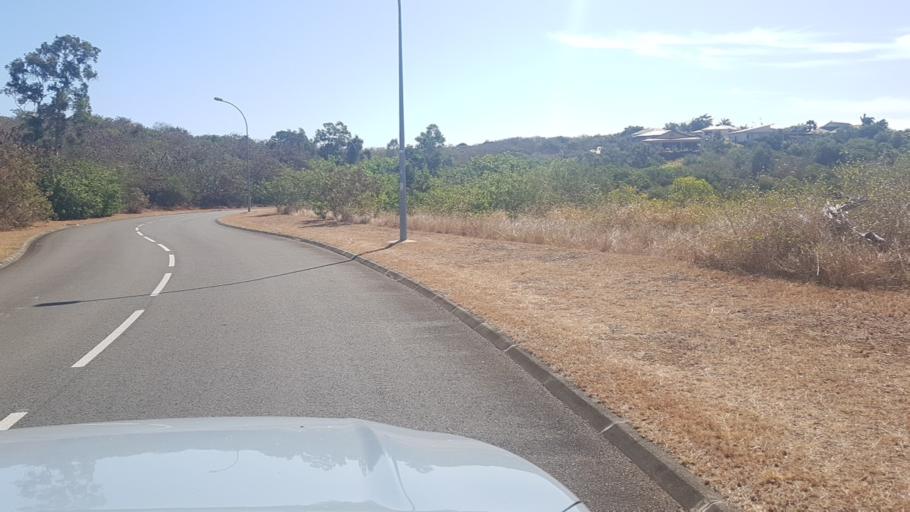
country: NC
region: South Province
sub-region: Dumbea
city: Dumbea
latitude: -22.1946
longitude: 166.4297
